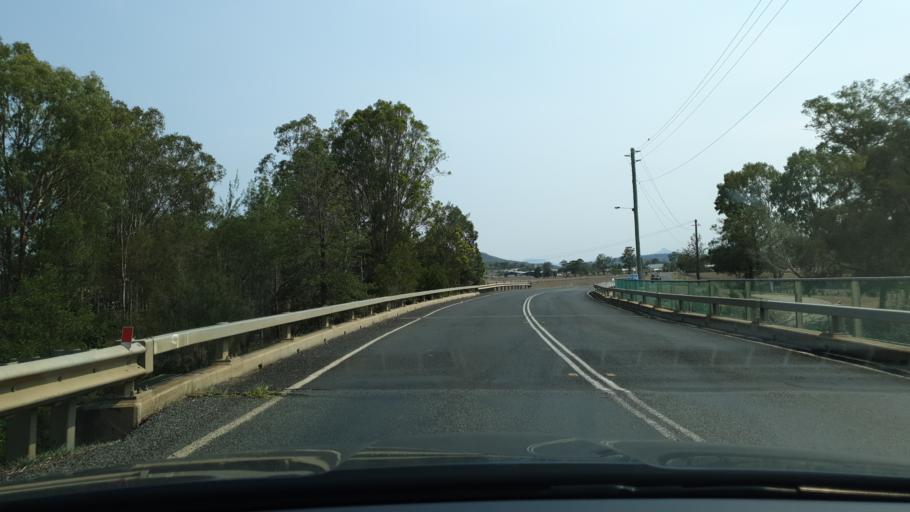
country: AU
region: Queensland
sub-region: Ipswich
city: Deebing Heights
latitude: -28.0074
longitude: 152.6803
